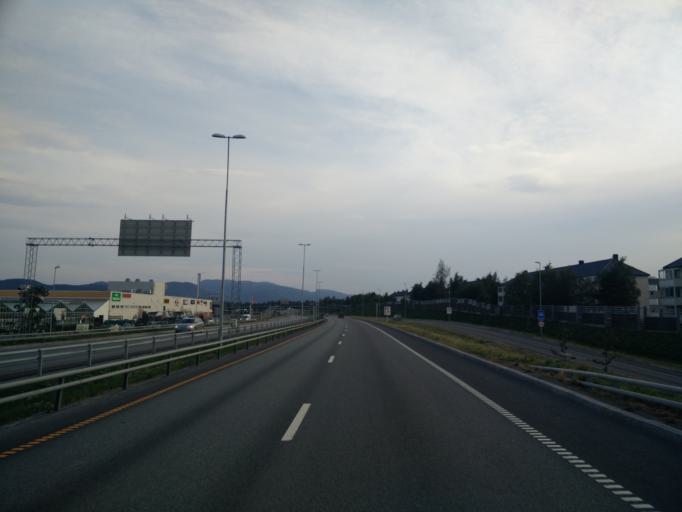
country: NO
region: Sor-Trondelag
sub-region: Trondheim
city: Trondheim
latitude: 63.3600
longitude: 10.3723
